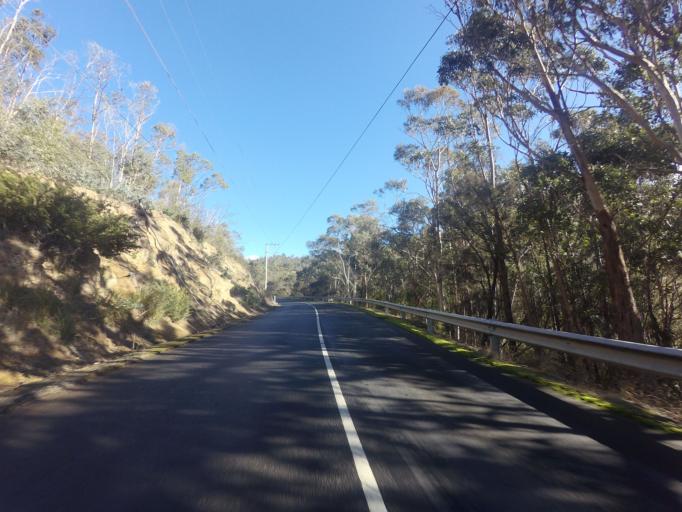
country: AU
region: Tasmania
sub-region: Glenorchy
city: Berriedale
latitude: -42.8194
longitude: 147.2169
